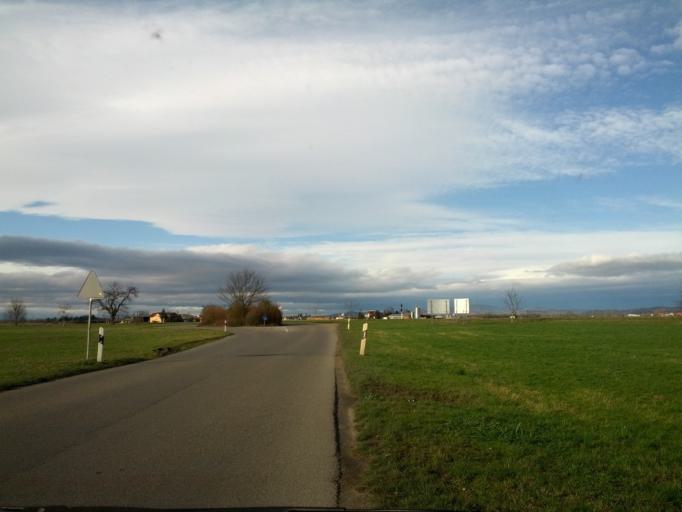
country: DE
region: Baden-Wuerttemberg
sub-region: Freiburg Region
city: Hartheim
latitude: 47.9155
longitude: 7.6324
